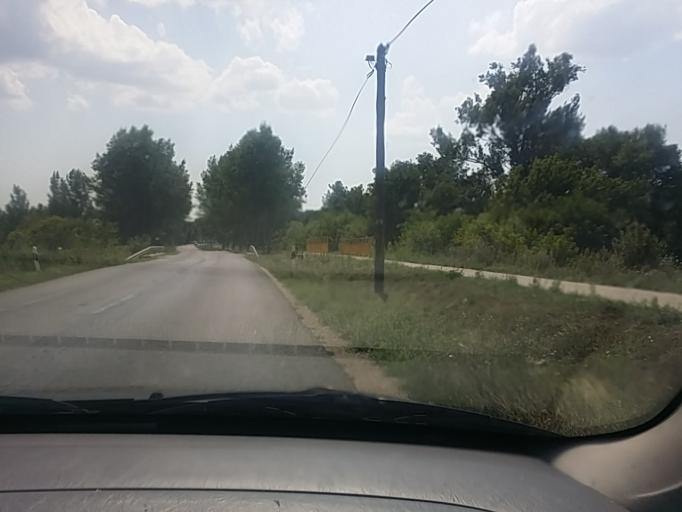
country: HU
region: Tolna
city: Dombovar
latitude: 46.3598
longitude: 18.1255
